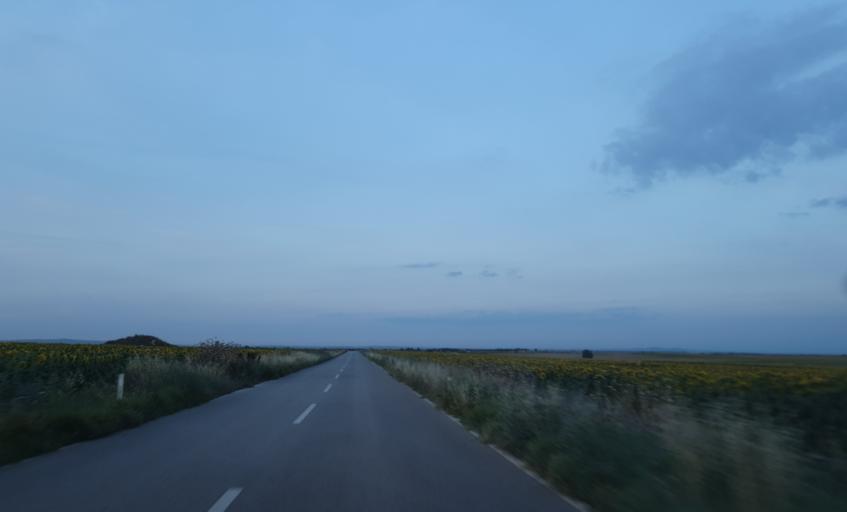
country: TR
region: Tekirdag
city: Beyazkoy
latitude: 41.4251
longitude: 27.6767
